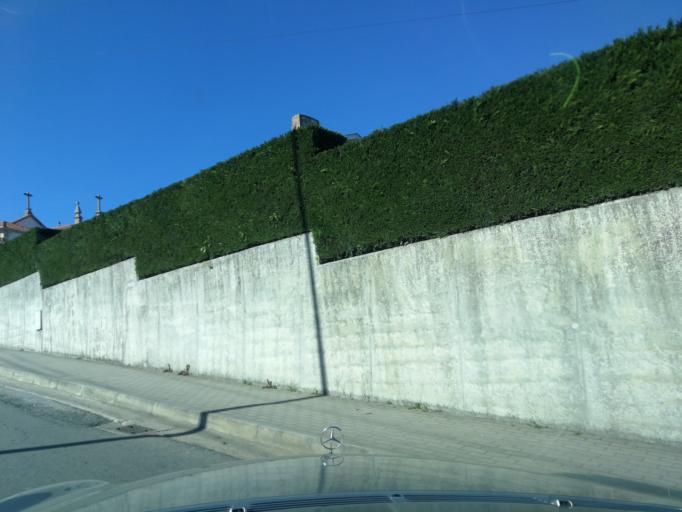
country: PT
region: Braga
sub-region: Vila Nova de Famalicao
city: Calendario
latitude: 41.4000
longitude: -8.5240
